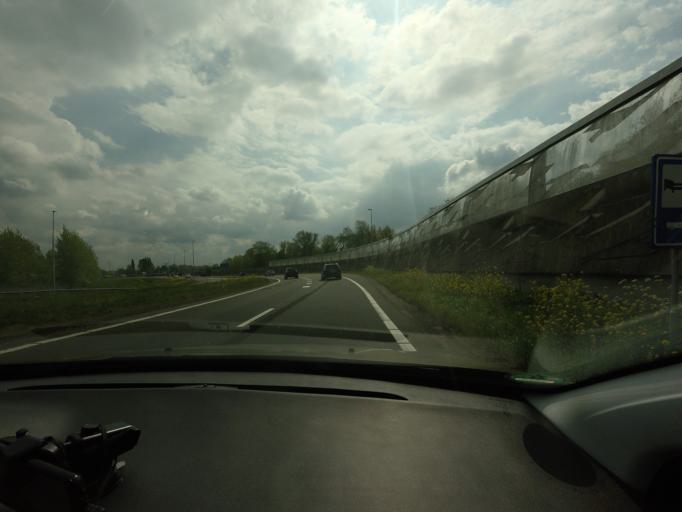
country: NL
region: Utrecht
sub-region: Stichtse Vecht
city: Vreeland
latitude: 52.2269
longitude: 4.9813
